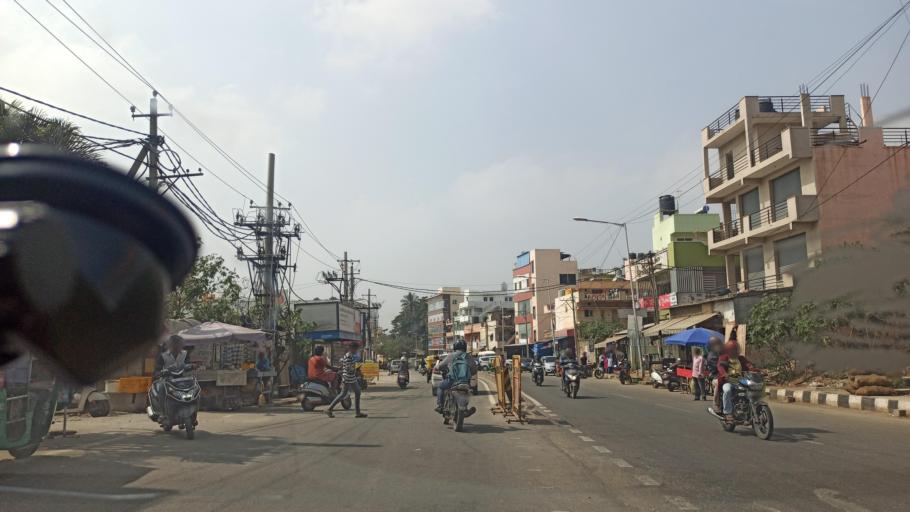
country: IN
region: Karnataka
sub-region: Bangalore Urban
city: Yelahanka
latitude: 13.1044
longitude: 77.6051
